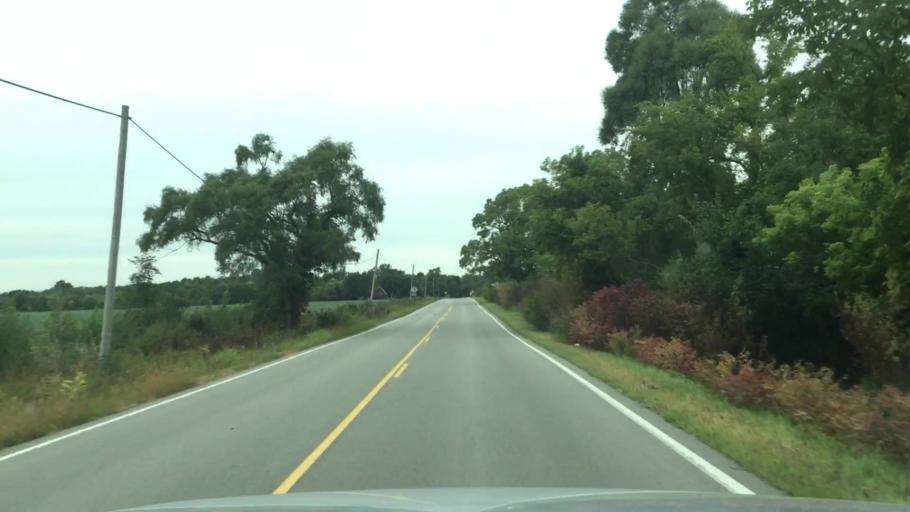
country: US
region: Michigan
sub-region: Washtenaw County
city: Milan
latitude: 42.0908
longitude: -83.7352
